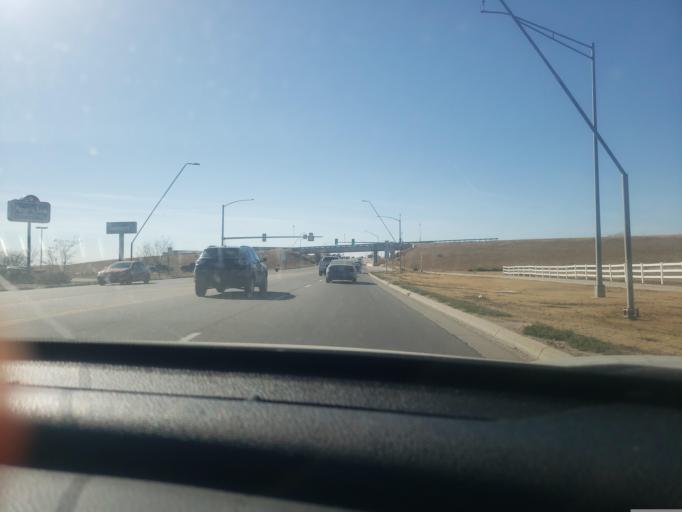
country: US
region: Kansas
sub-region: Finney County
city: Garden City
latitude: 37.9845
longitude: -100.8363
